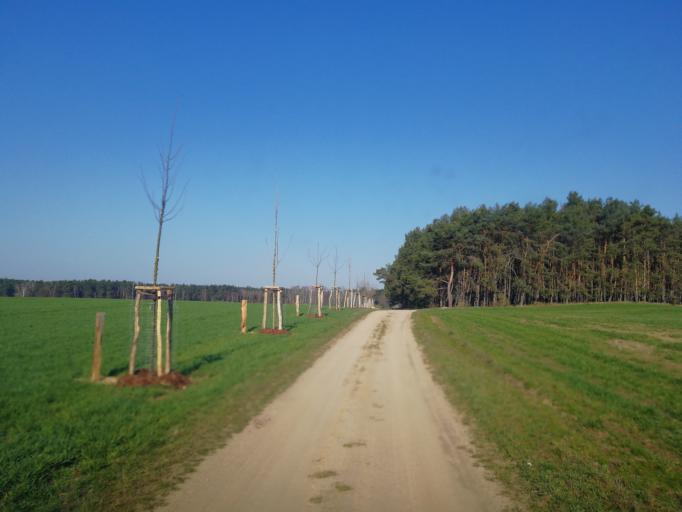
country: DE
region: Brandenburg
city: Drahnsdorf
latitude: 51.8345
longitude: 13.5885
